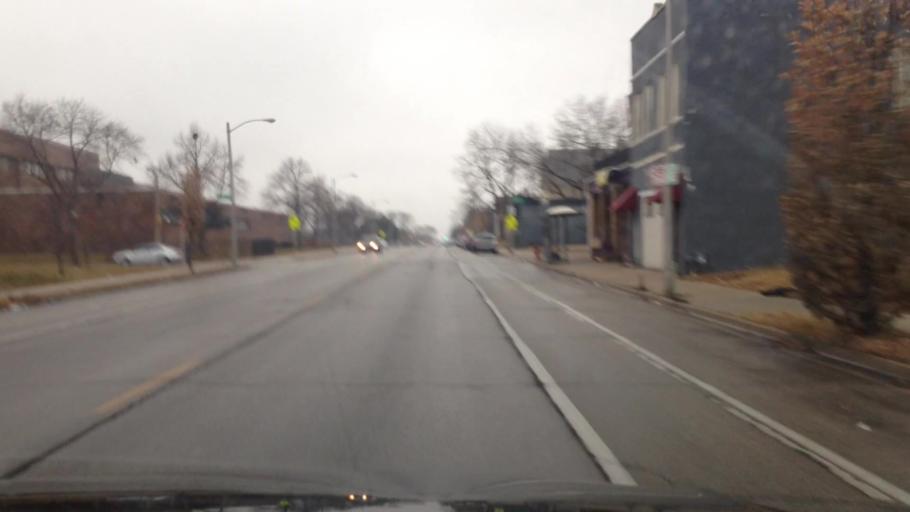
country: US
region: Wisconsin
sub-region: Milwaukee County
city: Milwaukee
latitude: 43.0677
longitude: -87.9233
